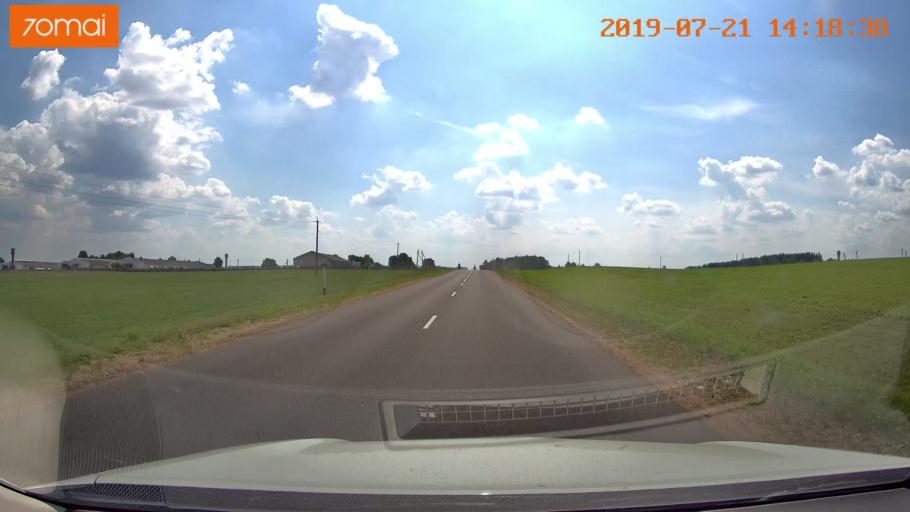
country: BY
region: Grodnenskaya
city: Karelichy
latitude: 53.5931
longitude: 26.1777
